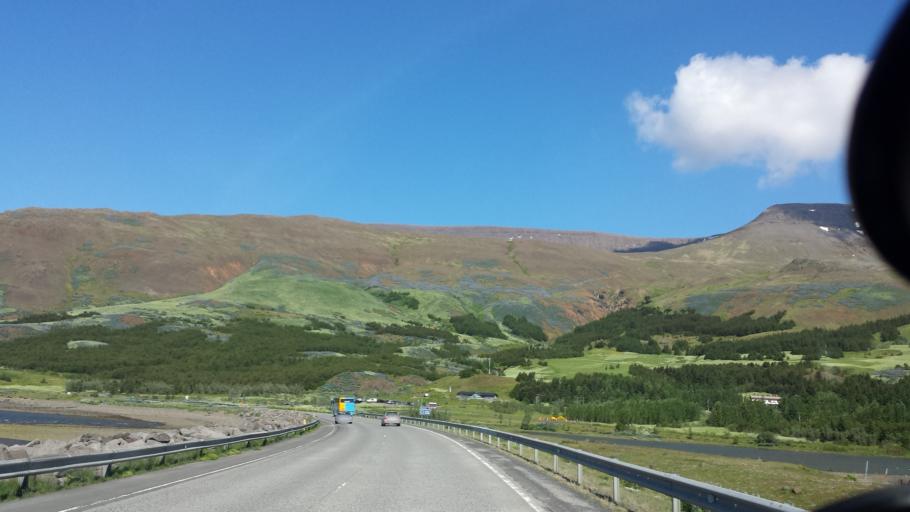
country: IS
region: Capital Region
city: Mosfellsbaer
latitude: 64.2057
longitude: -21.7089
